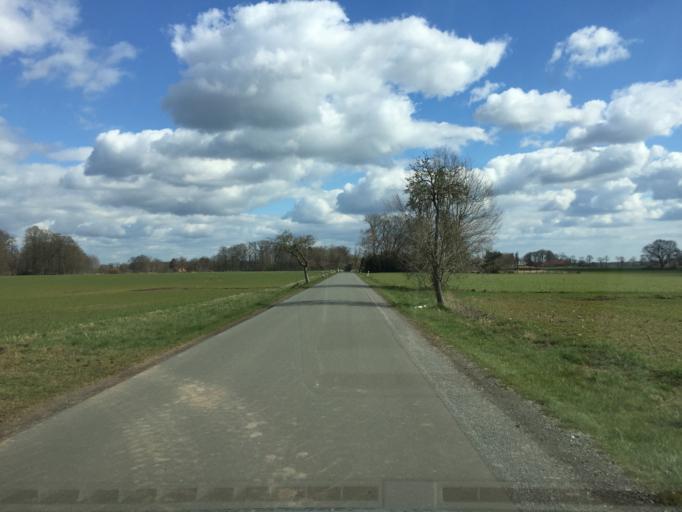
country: DE
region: Lower Saxony
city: Engeln
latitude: 52.7594
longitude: 8.9393
